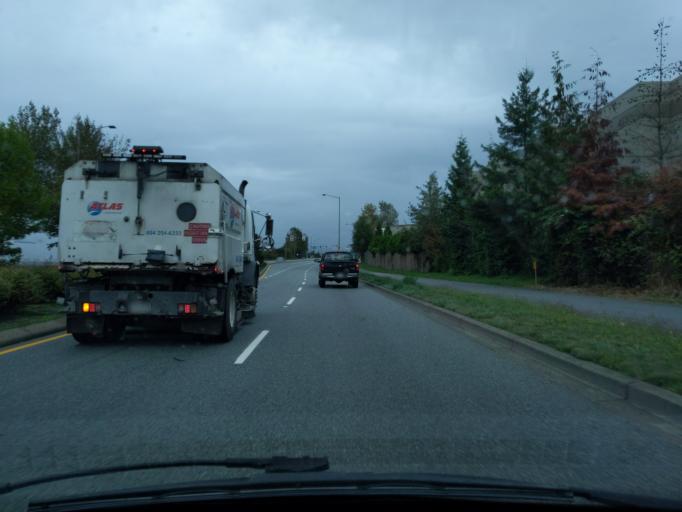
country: CA
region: British Columbia
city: Pitt Meadows
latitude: 49.1808
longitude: -122.6948
